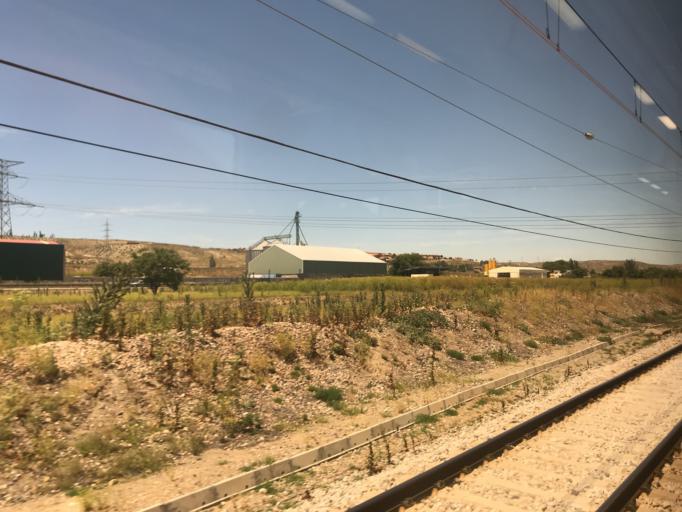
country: ES
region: Madrid
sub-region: Provincia de Madrid
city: Ciempozuelos
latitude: 40.0977
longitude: -3.6279
